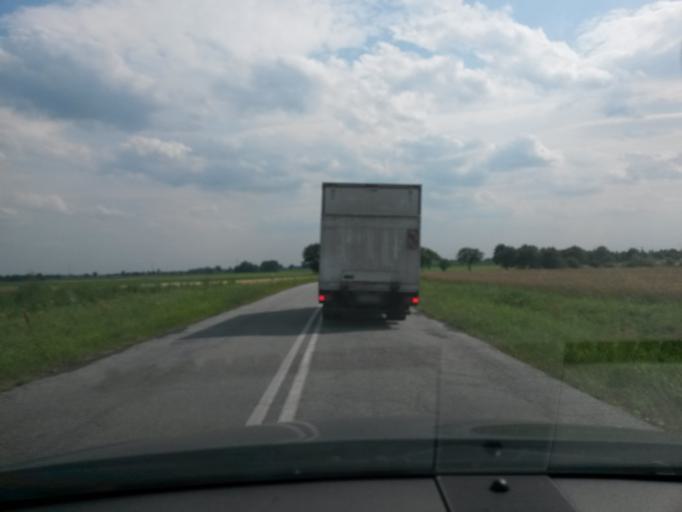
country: PL
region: Greater Poland Voivodeship
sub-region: Powiat poznanski
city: Kornik
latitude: 52.2964
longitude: 17.1228
